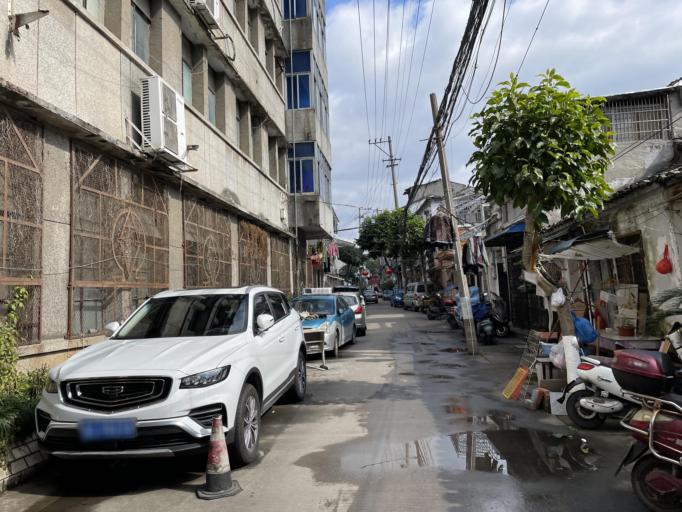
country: CN
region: Zhejiang Sheng
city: Wuma
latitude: 28.0200
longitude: 120.6485
